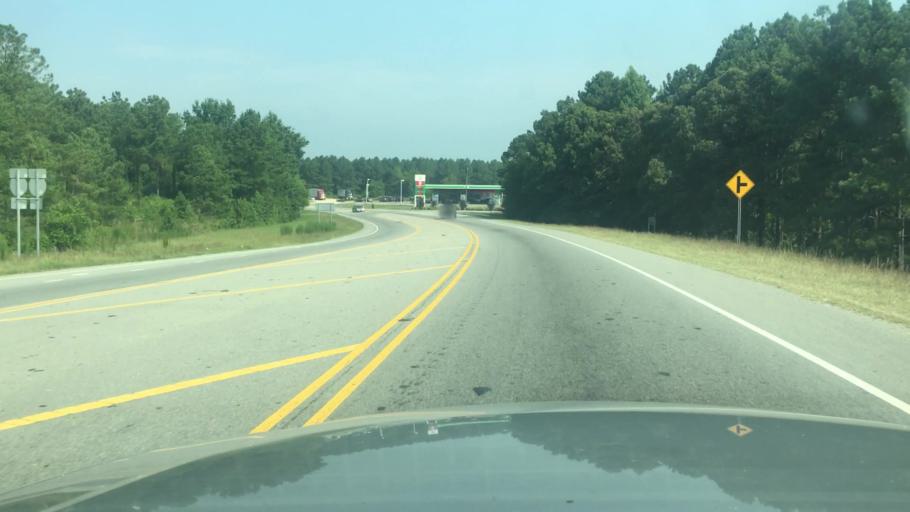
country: US
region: North Carolina
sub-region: Cumberland County
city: Hope Mills
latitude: 34.9397
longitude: -78.9236
